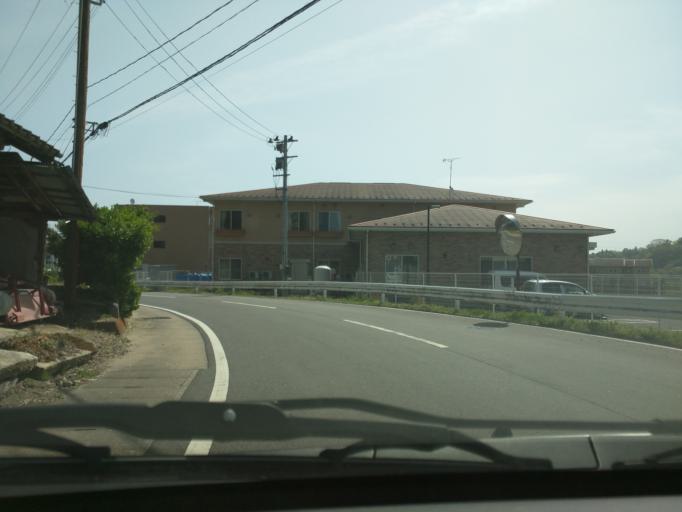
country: JP
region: Fukushima
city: Nihommatsu
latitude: 37.5845
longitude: 140.4461
